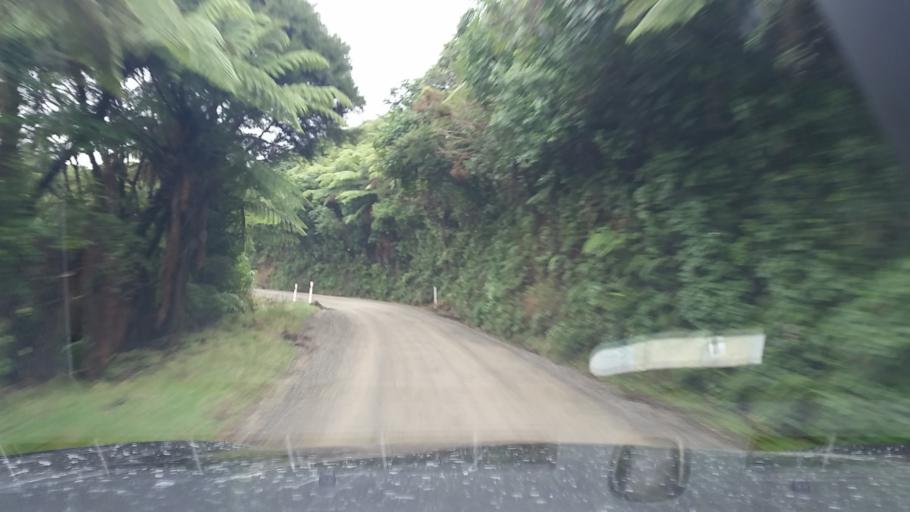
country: NZ
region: Marlborough
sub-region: Marlborough District
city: Picton
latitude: -41.1789
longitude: 173.9875
